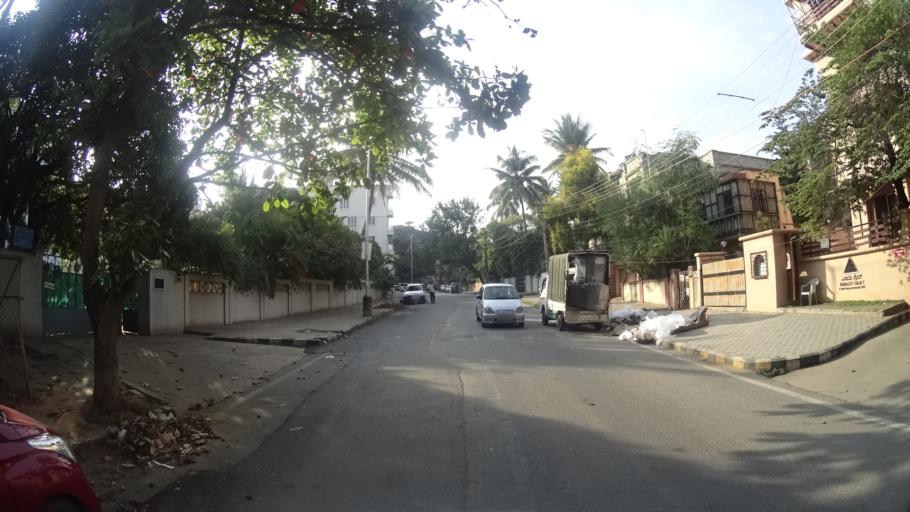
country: IN
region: Karnataka
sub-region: Bangalore Urban
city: Bangalore
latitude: 13.0034
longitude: 77.6211
